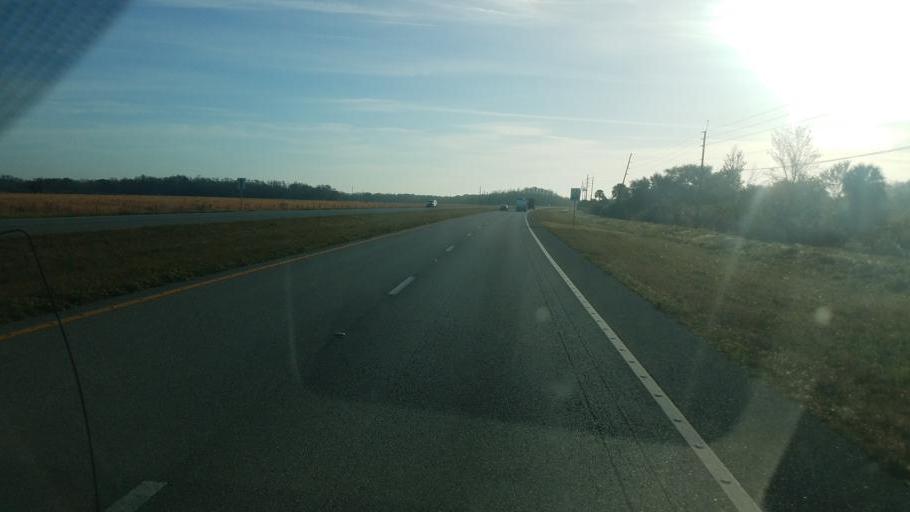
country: US
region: Florida
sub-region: Osceola County
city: Saint Cloud
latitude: 28.1447
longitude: -81.0736
